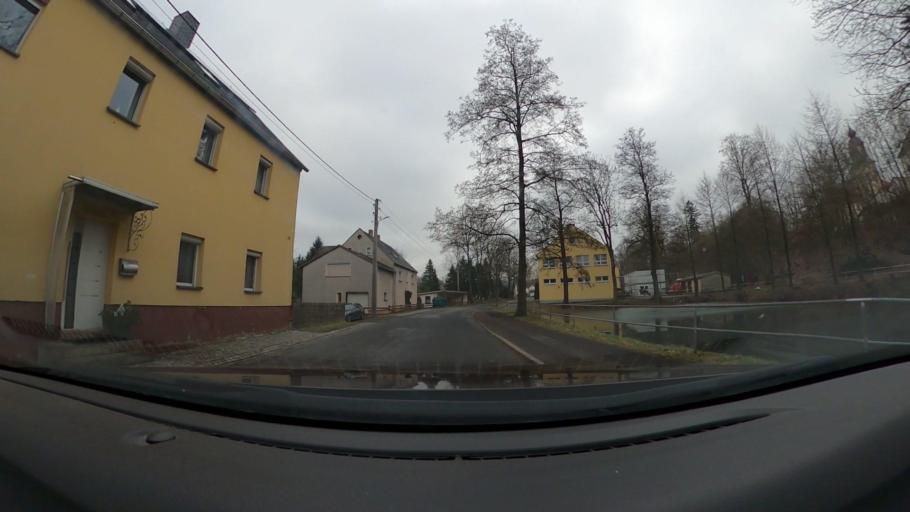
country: DE
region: Saxony
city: Oberschona
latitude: 50.8969
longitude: 13.2543
